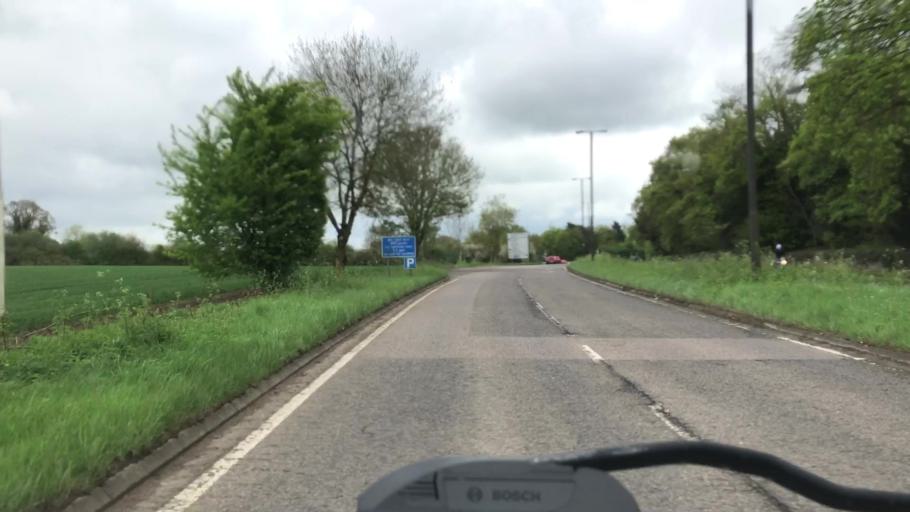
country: GB
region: England
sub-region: Gloucestershire
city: Cirencester
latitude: 51.7195
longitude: -1.9617
